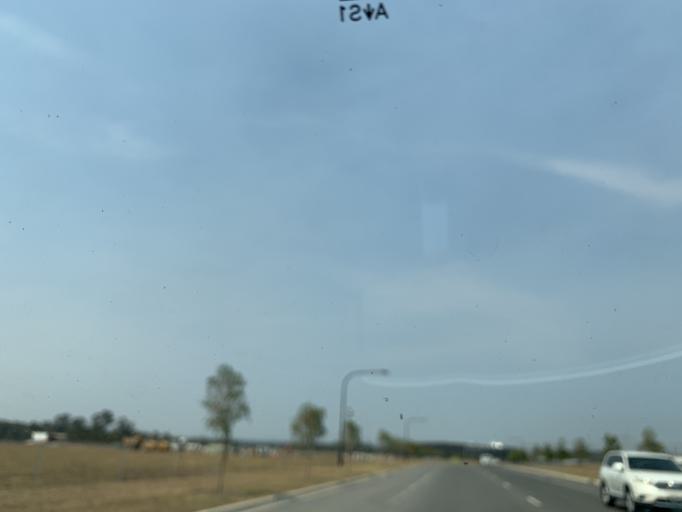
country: AU
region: New South Wales
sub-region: Blacktown
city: Hassall Grove
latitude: -33.7174
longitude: 150.8315
